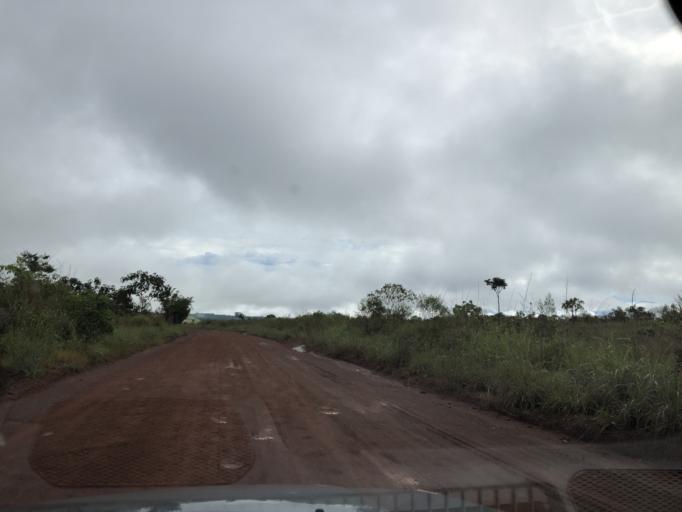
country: BR
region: Federal District
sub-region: Brasilia
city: Brasilia
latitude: -15.6128
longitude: -48.0455
